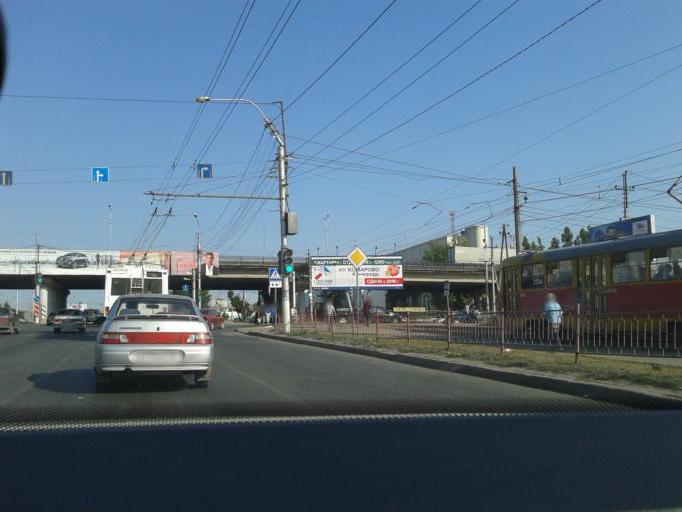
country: RU
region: Volgograd
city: Volgograd
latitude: 48.7532
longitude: 44.4830
